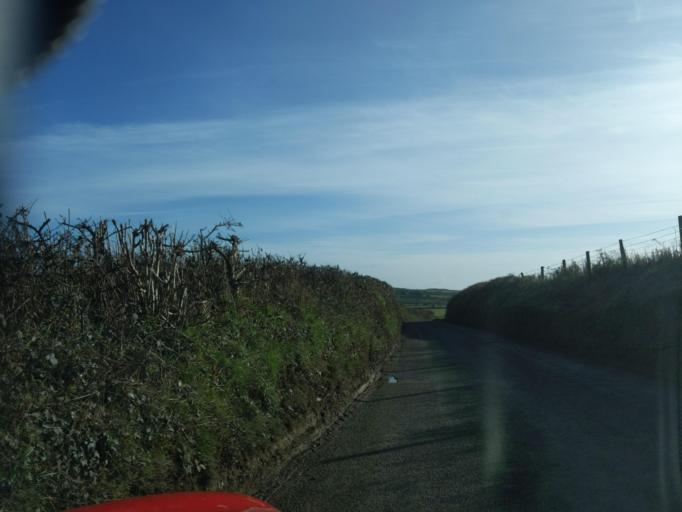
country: GB
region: England
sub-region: Devon
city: Kingsbridge
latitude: 50.3408
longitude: -3.7242
